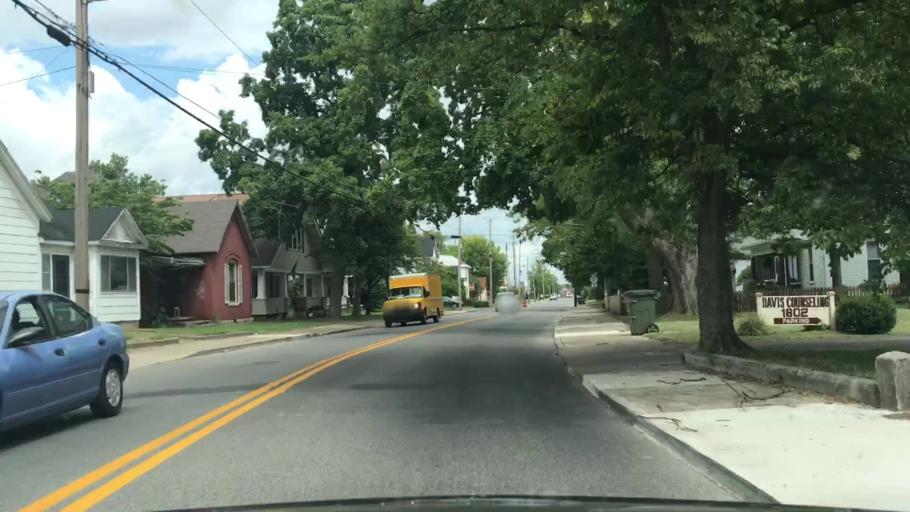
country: US
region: Kentucky
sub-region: Christian County
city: Hopkinsville
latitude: 36.8587
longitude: -87.4923
